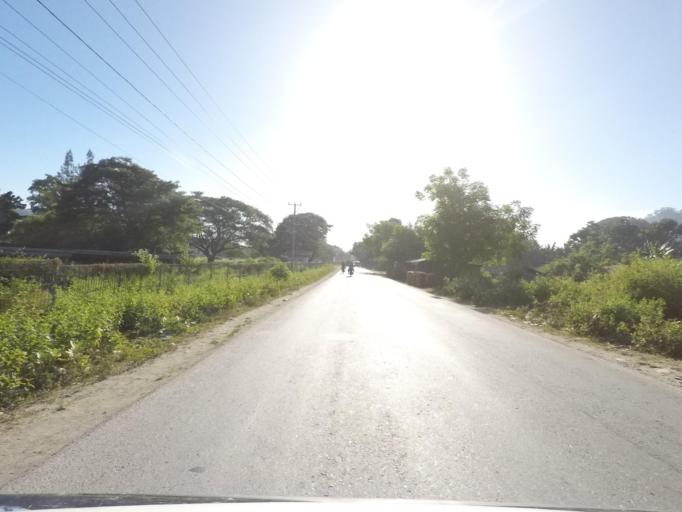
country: TL
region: Dili
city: Dili
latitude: -8.5527
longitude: 125.6598
